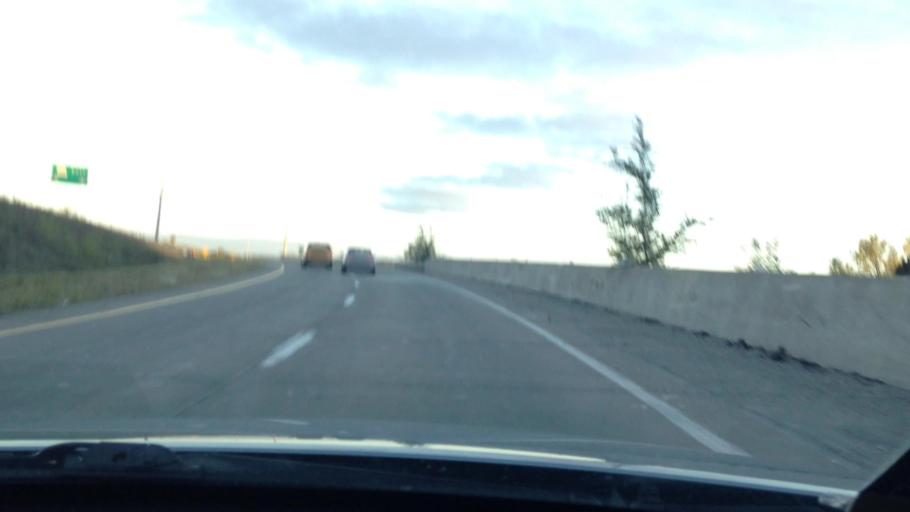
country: US
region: Missouri
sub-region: Jackson County
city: Raytown
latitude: 39.0187
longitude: -94.5004
